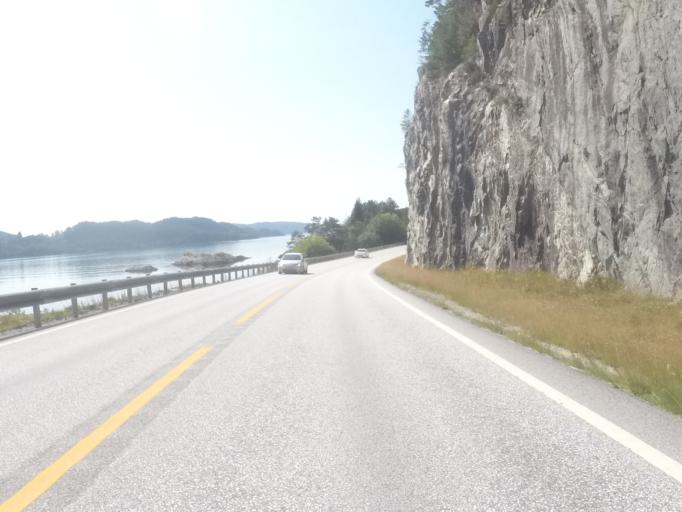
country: NO
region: Sogn og Fjordane
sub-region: Bremanger
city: Svelgen
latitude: 61.6104
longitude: 5.2261
